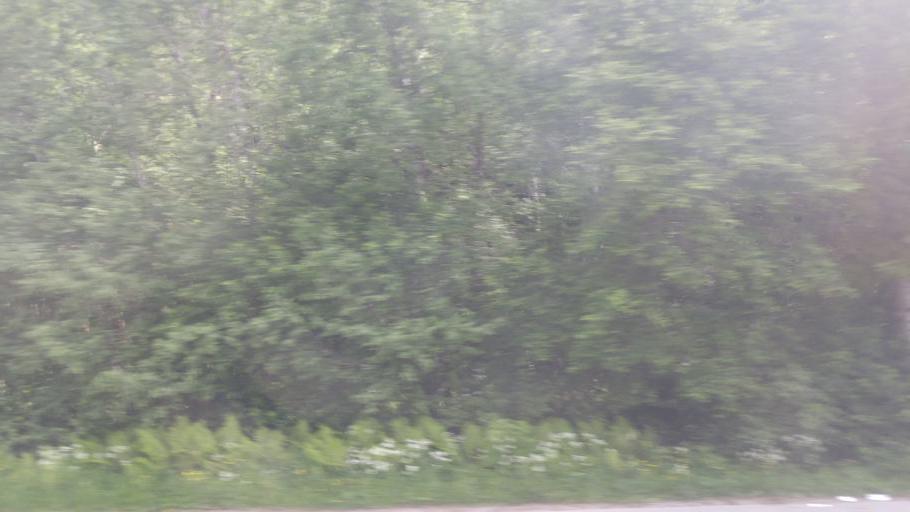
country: NO
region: Sor-Trondelag
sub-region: Midtre Gauldal
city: Storen
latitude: 63.0375
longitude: 10.2983
